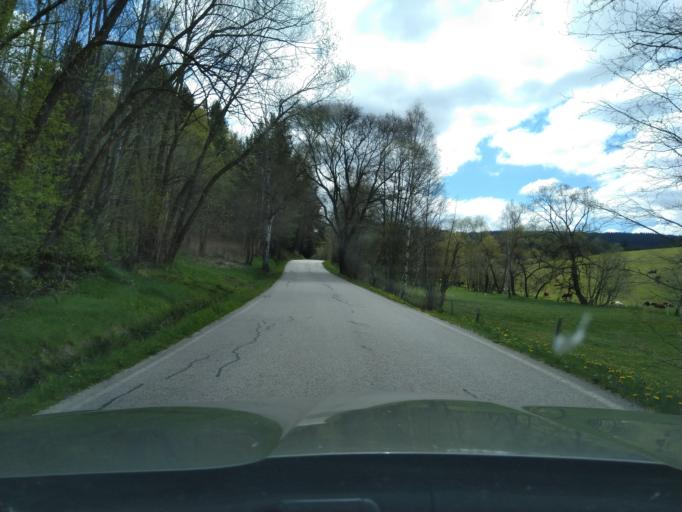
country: CZ
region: Jihocesky
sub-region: Okres Prachatice
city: Vimperk
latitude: 49.0334
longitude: 13.7583
